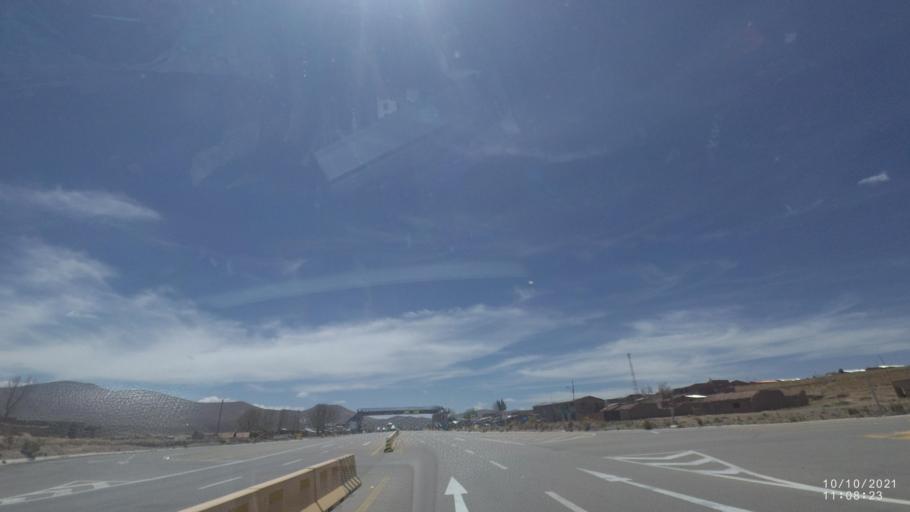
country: BO
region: La Paz
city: Colquiri
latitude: -17.6679
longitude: -67.0520
